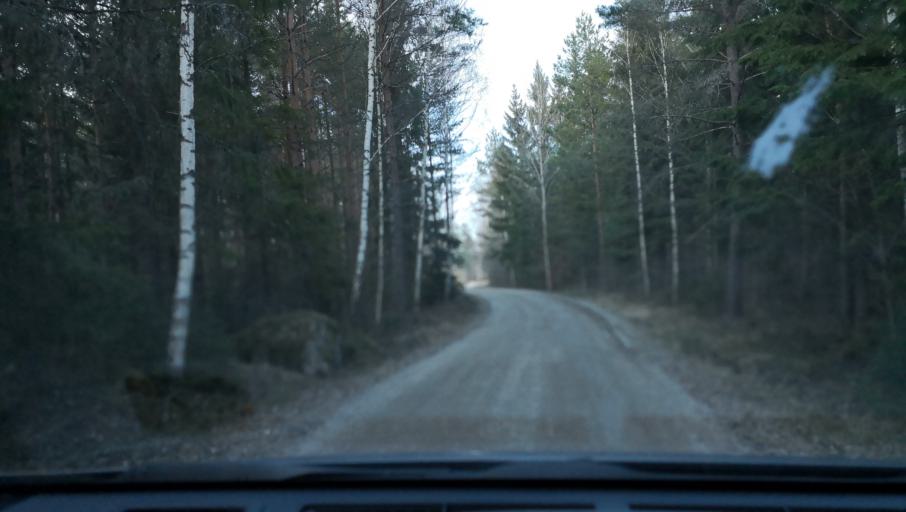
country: SE
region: OErebro
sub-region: Lindesbergs Kommun
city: Frovi
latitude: 59.3800
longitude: 15.3607
